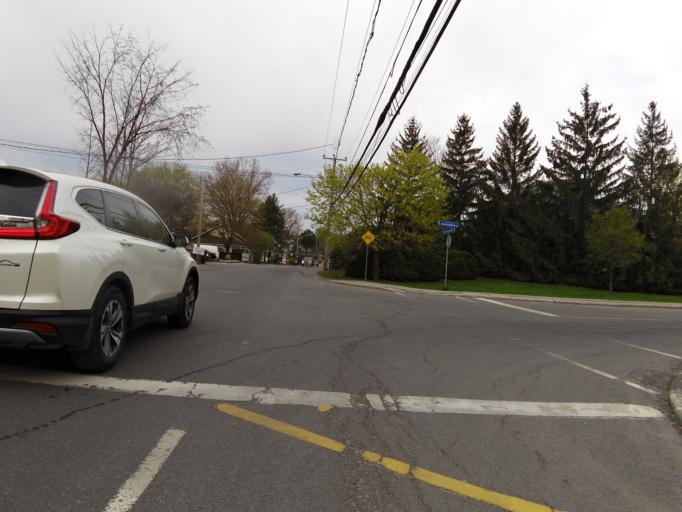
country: CA
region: Quebec
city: Dollard-Des Ormeaux
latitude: 45.5209
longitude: -73.8341
